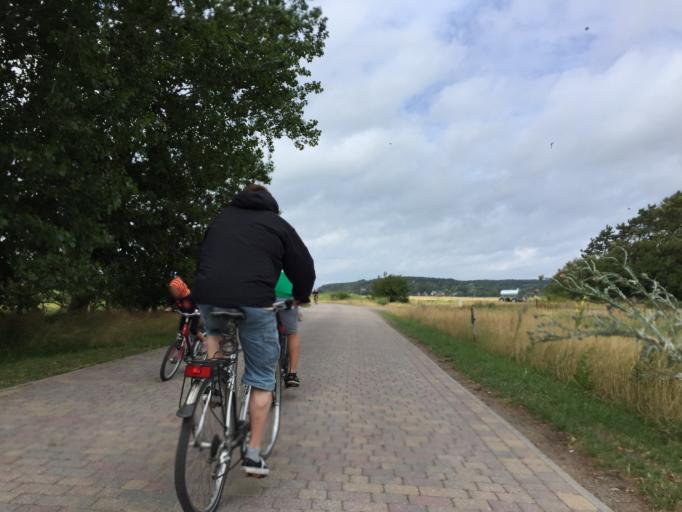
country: DE
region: Mecklenburg-Vorpommern
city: Hiddensee
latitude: 54.5733
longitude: 13.1063
